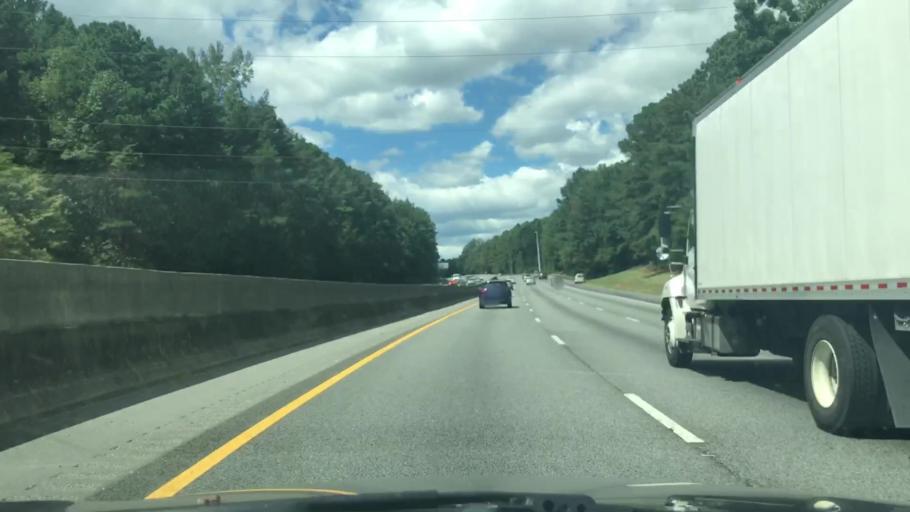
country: US
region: Georgia
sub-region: DeKalb County
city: Stone Mountain
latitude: 33.8228
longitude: -84.1721
